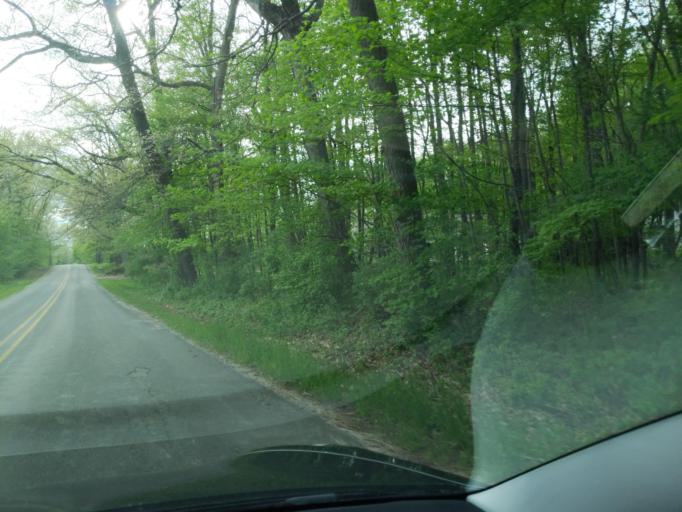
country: US
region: Michigan
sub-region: Ingham County
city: Stockbridge
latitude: 42.4392
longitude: -84.1440
